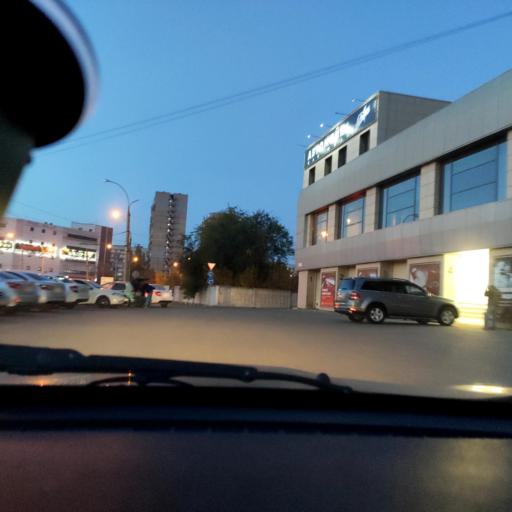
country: RU
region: Samara
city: Tol'yatti
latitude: 53.5240
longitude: 49.3276
